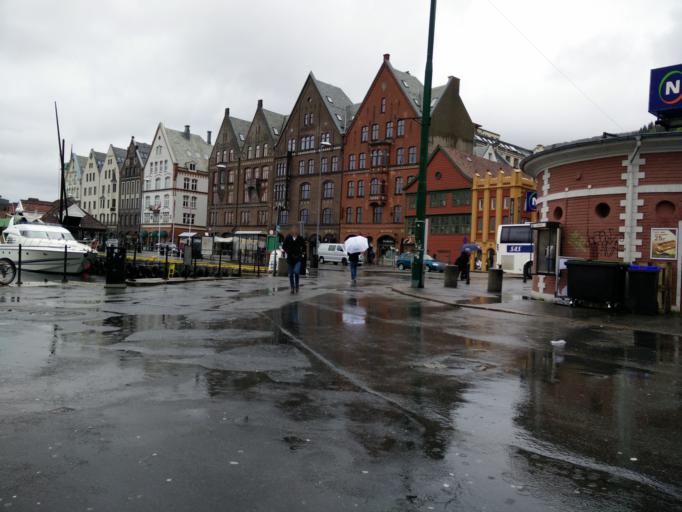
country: NO
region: Hordaland
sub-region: Bergen
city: Bergen
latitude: 60.3953
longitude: 5.3256
